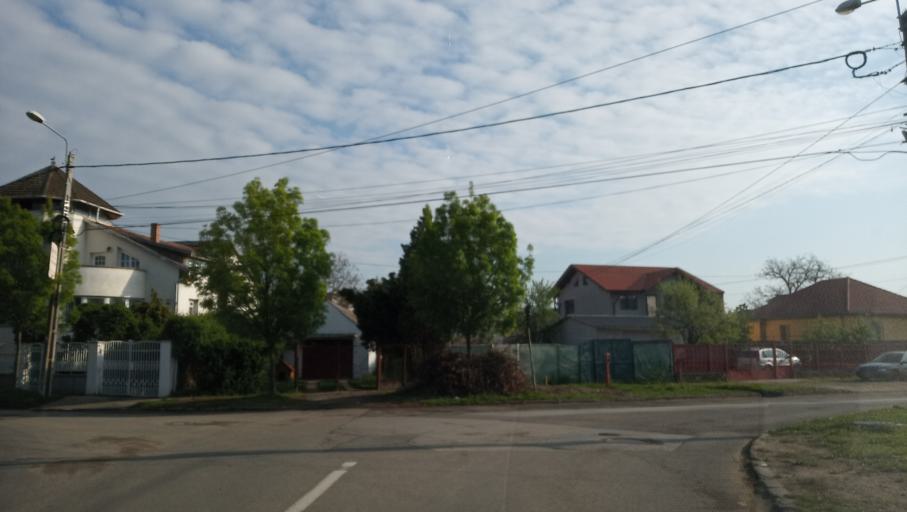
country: RO
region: Timis
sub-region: Comuna Ghiroda
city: Ghiroda
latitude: 45.7652
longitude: 21.2636
